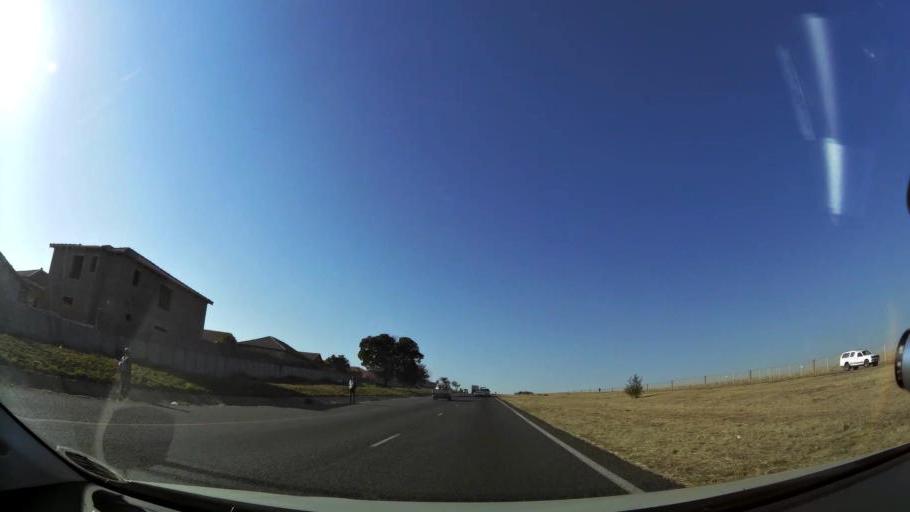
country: ZA
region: Gauteng
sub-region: City of Johannesburg Metropolitan Municipality
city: Modderfontein
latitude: -26.0536
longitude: 28.1618
